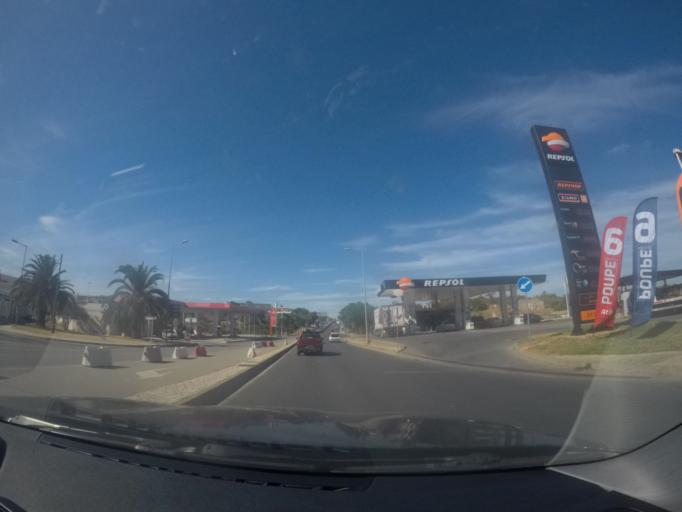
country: PT
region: Faro
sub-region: Portimao
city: Portimao
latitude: 37.1498
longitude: -8.5401
